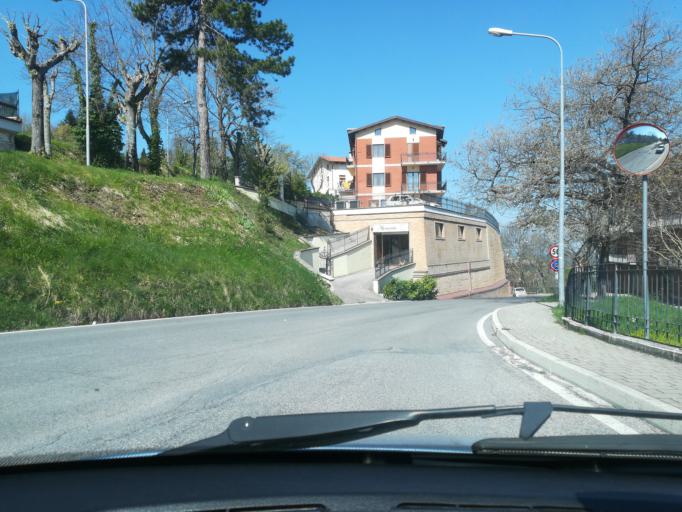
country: IT
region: The Marches
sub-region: Provincia di Macerata
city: Cingoli
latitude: 43.3754
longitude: 13.2076
